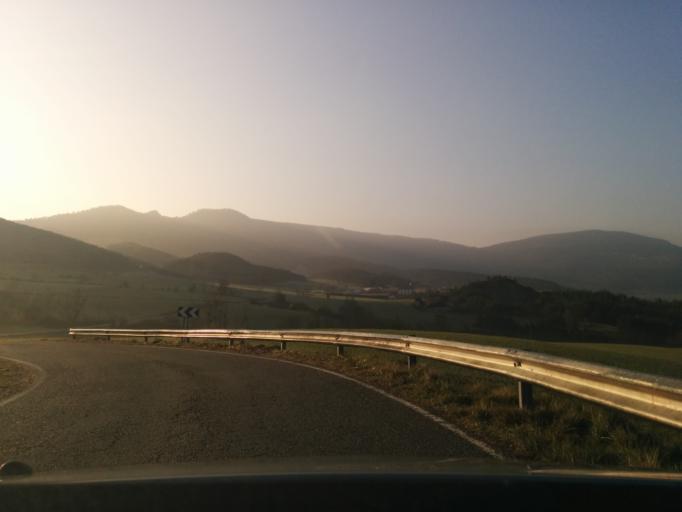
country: ES
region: Navarre
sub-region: Provincia de Navarra
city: Elorz
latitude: 42.7820
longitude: -1.5327
